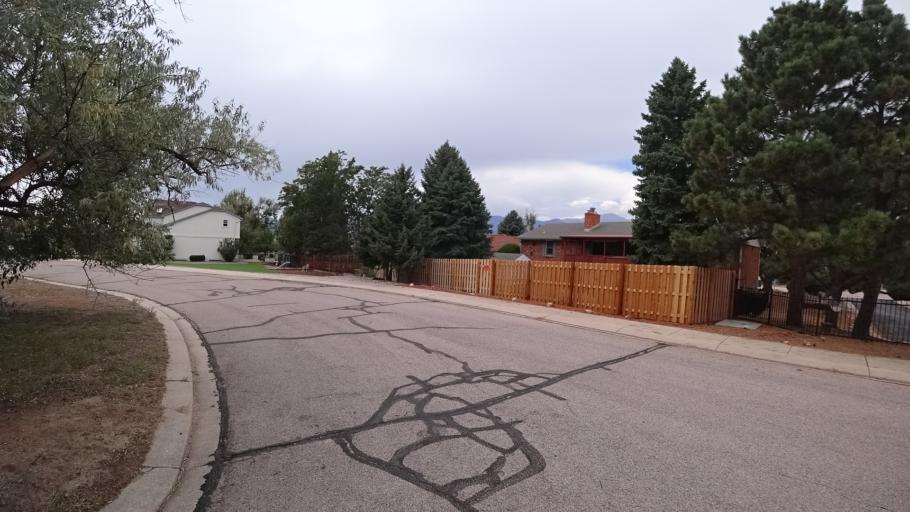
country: US
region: Colorado
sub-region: El Paso County
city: Colorado Springs
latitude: 38.8715
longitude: -104.7855
